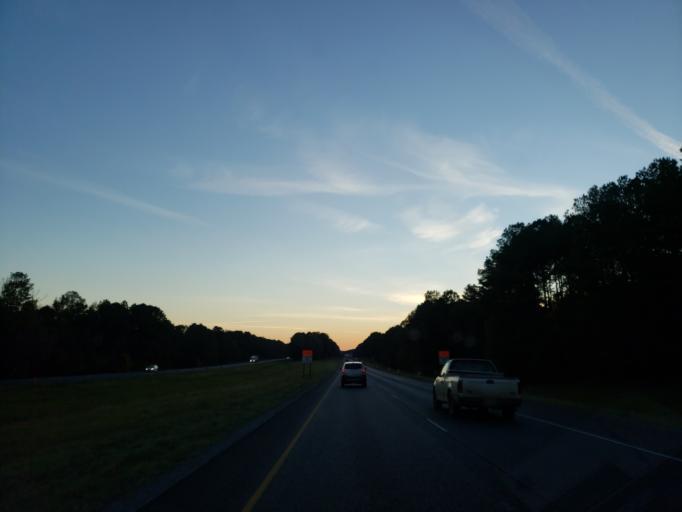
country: US
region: Alabama
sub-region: Sumter County
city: York
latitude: 32.5506
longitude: -88.2705
